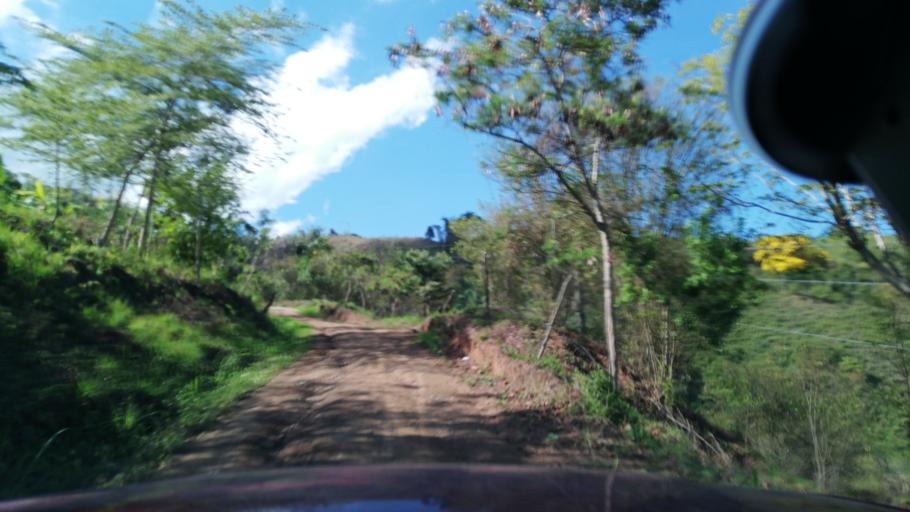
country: CO
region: Cundinamarca
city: Quipile
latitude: 4.7463
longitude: -74.6134
